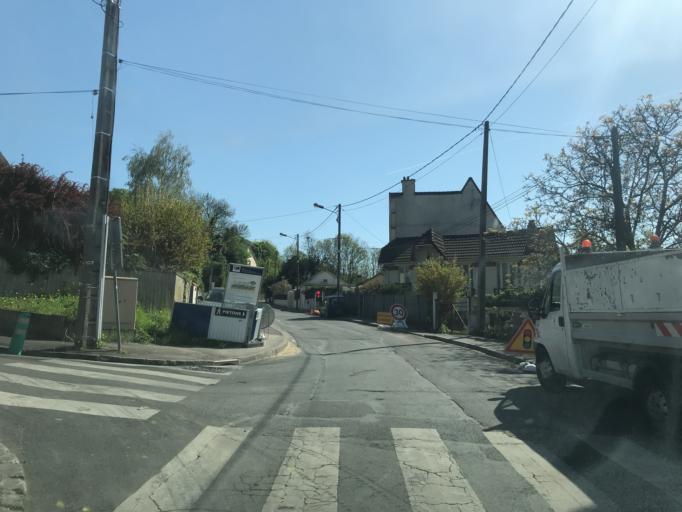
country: FR
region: Ile-de-France
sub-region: Departement du Val-de-Marne
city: Chennevieres-sur-Marne
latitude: 48.7942
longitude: 2.5260
